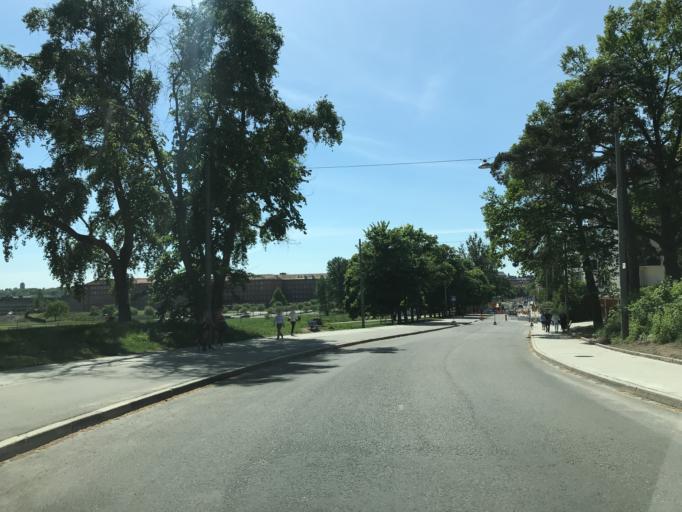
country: SE
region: Stockholm
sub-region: Stockholms Kommun
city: OEstermalm
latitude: 59.3451
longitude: 18.1015
